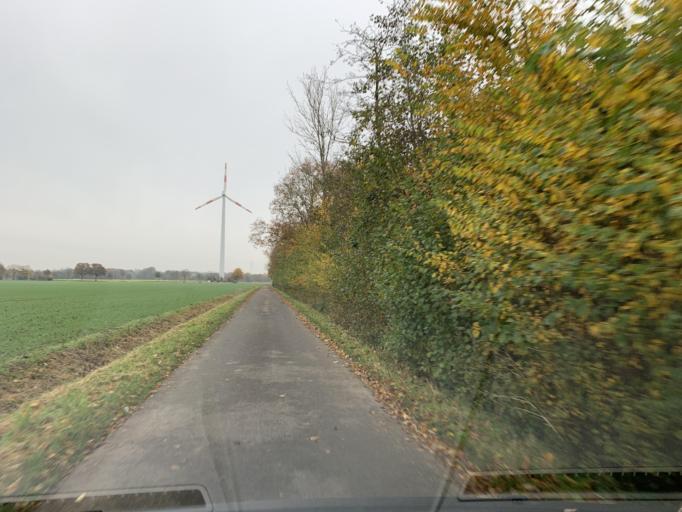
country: DE
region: North Rhine-Westphalia
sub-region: Regierungsbezirk Munster
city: Greven
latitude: 52.0369
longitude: 7.5707
